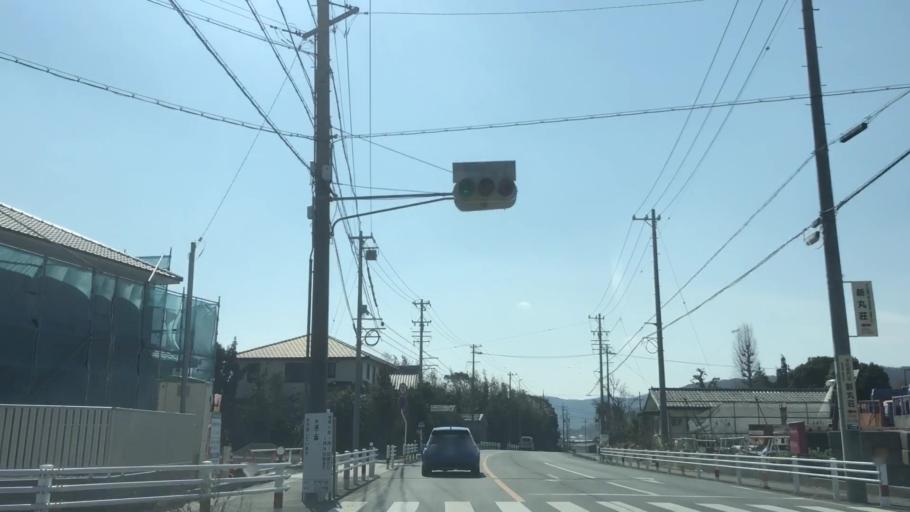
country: JP
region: Aichi
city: Tahara
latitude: 34.6461
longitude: 137.2412
